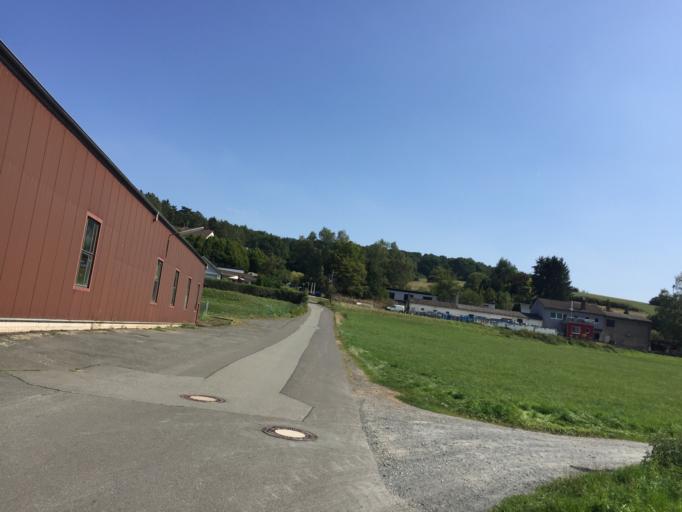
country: DE
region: Hesse
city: Solms
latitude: 50.5176
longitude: 8.4093
